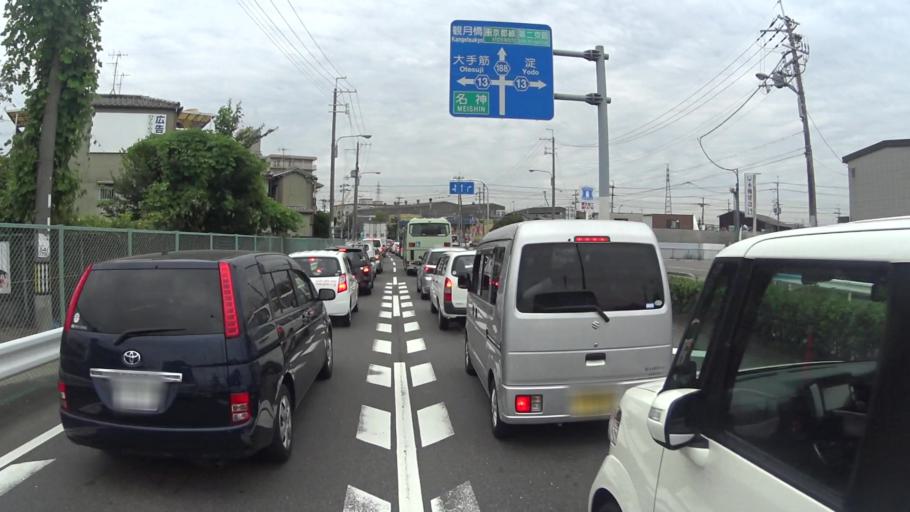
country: JP
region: Kyoto
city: Muko
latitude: 34.9281
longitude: 135.7388
